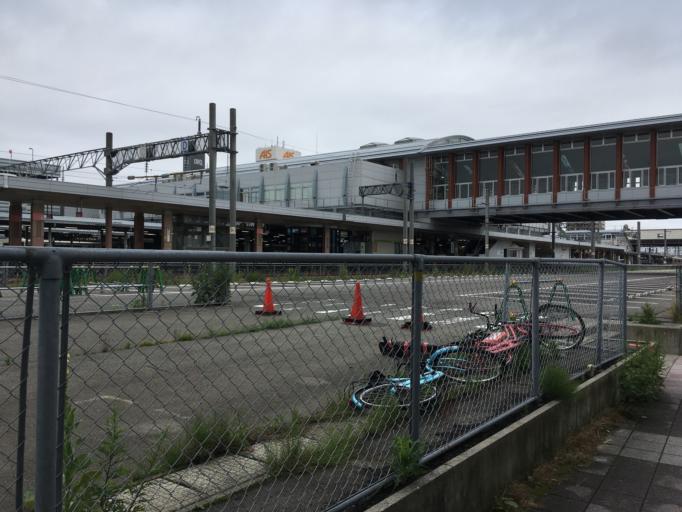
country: JP
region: Akita
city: Akita
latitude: 39.7161
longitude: 140.1304
